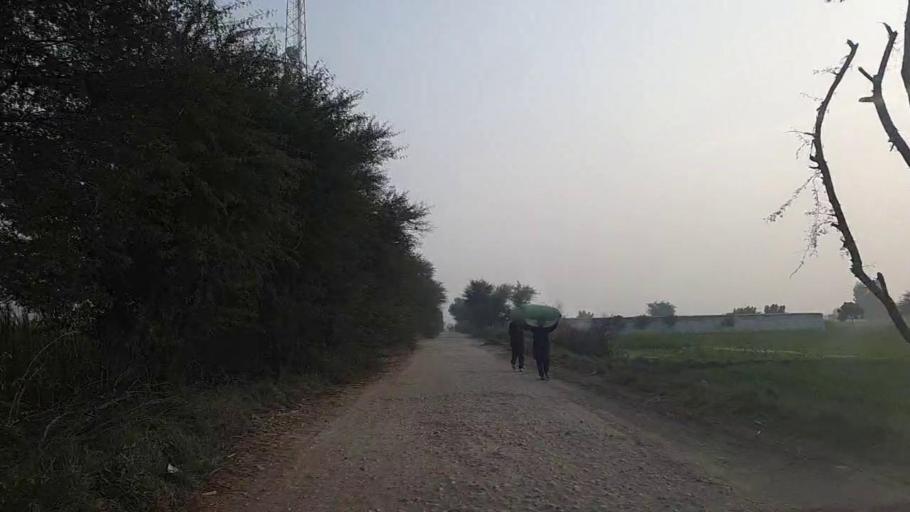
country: PK
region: Sindh
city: Khadro
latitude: 26.1217
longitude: 68.7960
